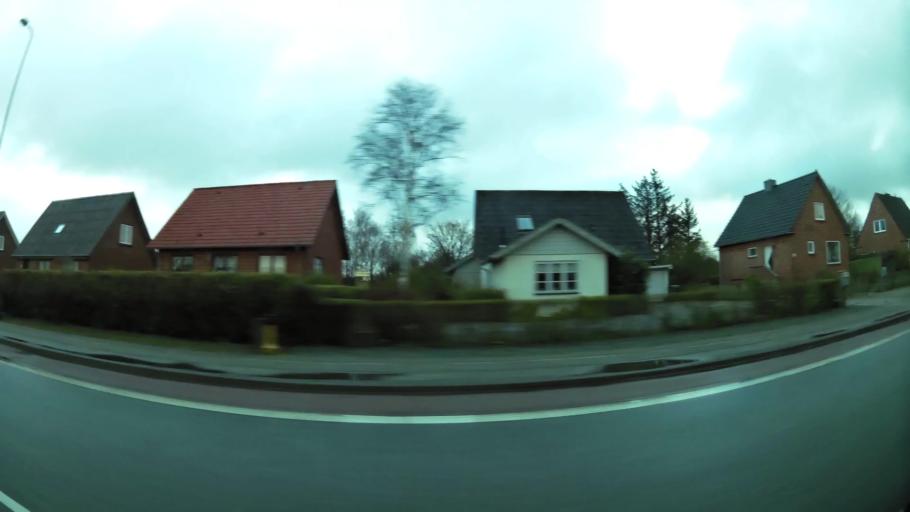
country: DK
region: Central Jutland
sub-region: Ringkobing-Skjern Kommune
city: Skjern
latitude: 55.9575
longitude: 8.4878
